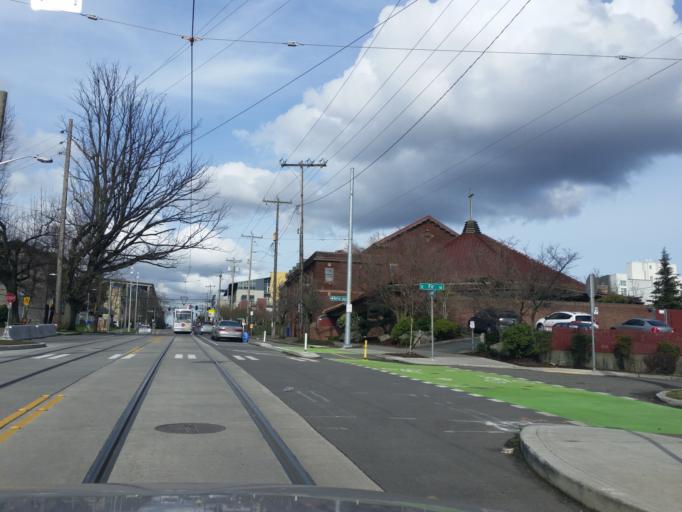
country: US
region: Washington
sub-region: King County
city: Seattle
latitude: 47.6026
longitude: -122.3208
